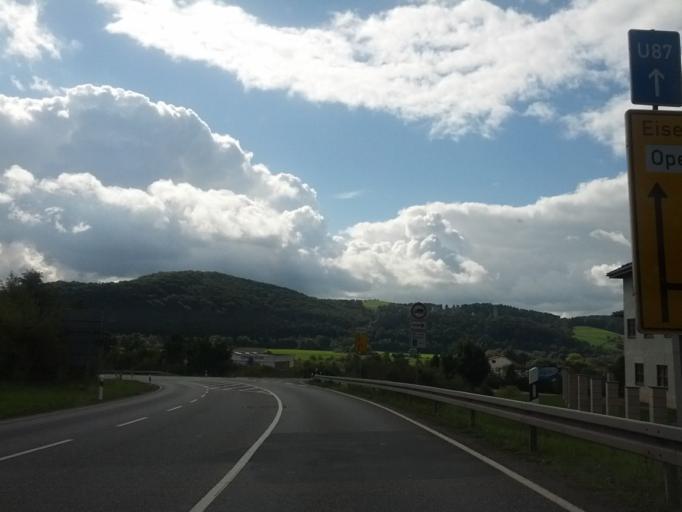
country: DE
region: Hesse
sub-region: Regierungsbezirk Kassel
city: Herleshausen
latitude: 51.0063
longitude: 10.1784
